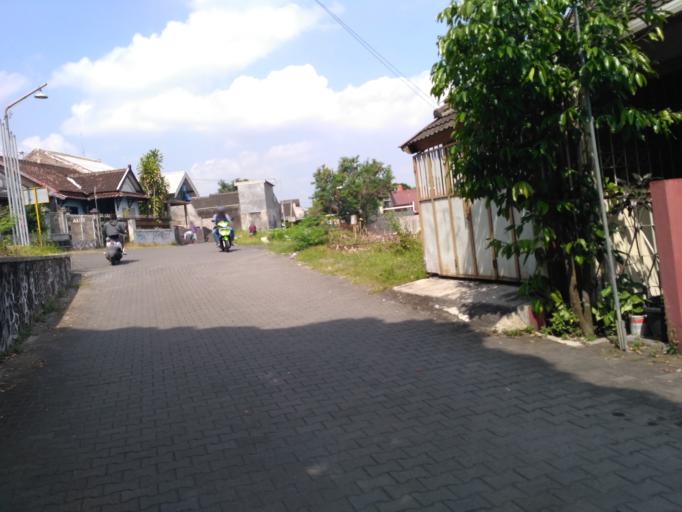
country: ID
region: Daerah Istimewa Yogyakarta
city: Depok
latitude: -7.7422
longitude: 110.4102
